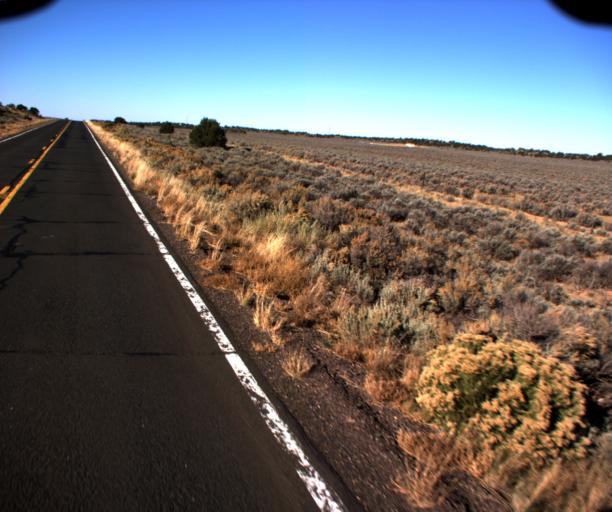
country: US
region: Arizona
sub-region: Navajo County
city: First Mesa
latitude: 35.7465
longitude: -110.0550
